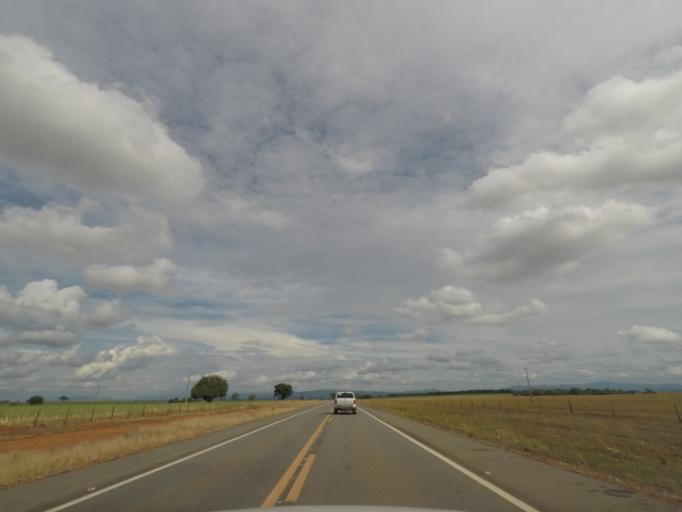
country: BR
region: Goias
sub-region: Uruacu
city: Uruacu
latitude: -14.6915
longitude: -49.1206
